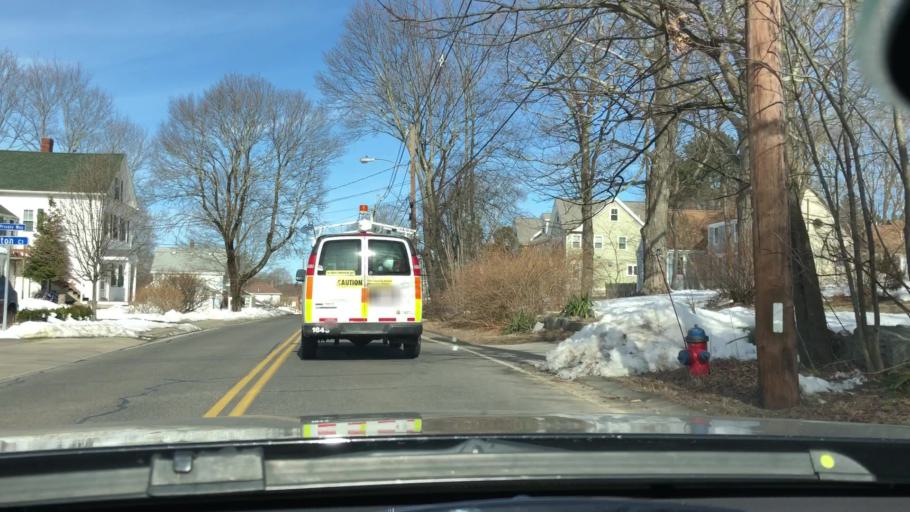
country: US
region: Massachusetts
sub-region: Norfolk County
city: Walpole
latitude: 42.1588
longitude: -71.2382
